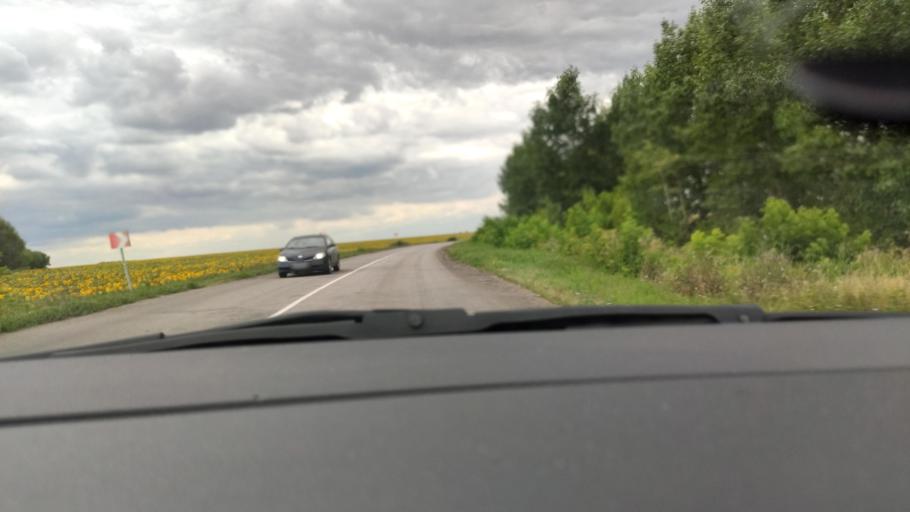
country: RU
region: Voronezj
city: Zemlyansk
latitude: 51.9371
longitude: 38.9795
